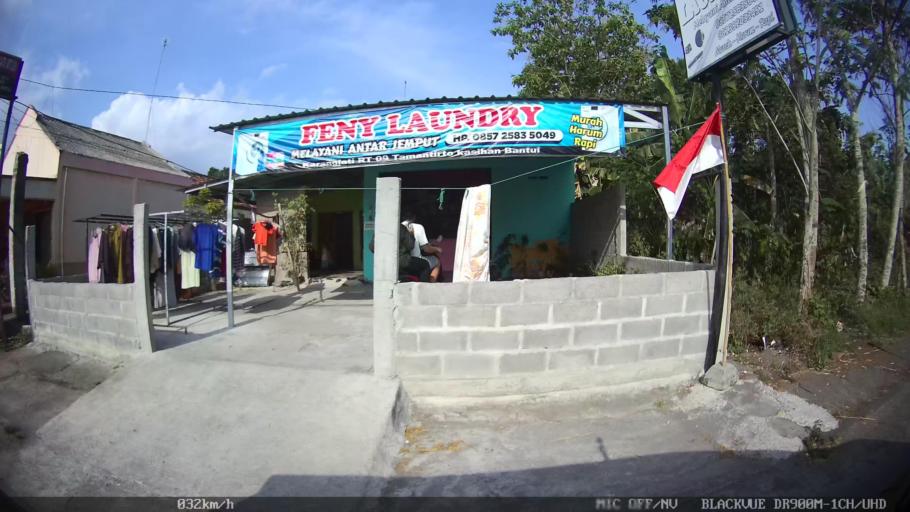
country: ID
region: Daerah Istimewa Yogyakarta
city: Kasihan
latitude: -7.8343
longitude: 110.3233
